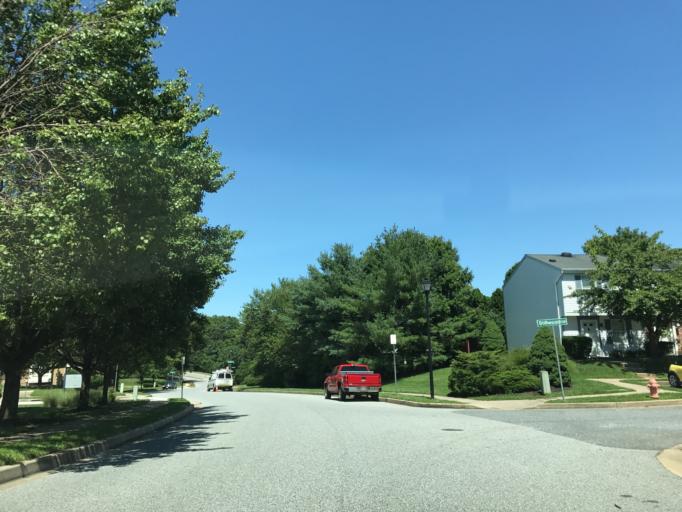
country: US
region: Maryland
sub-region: Baltimore County
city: White Marsh
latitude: 39.3817
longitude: -76.4628
